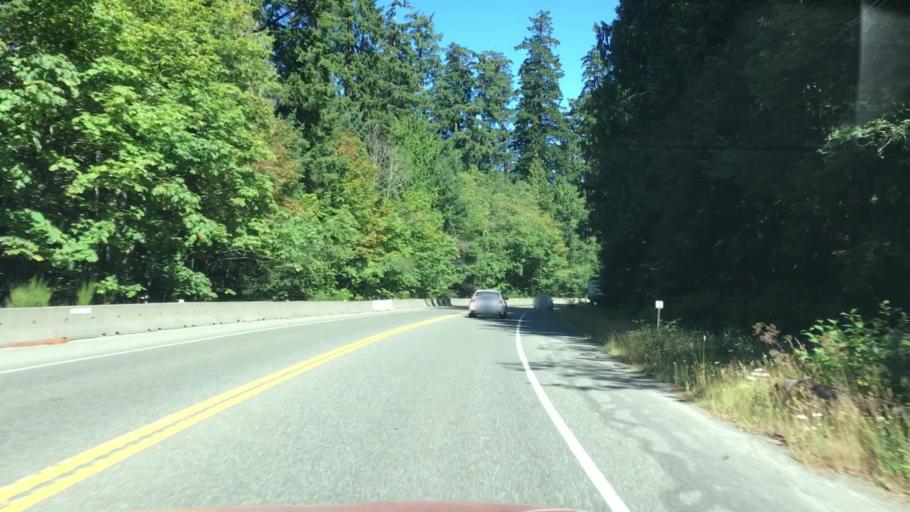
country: CA
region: British Columbia
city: Port Alberni
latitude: 49.2874
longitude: -124.5981
